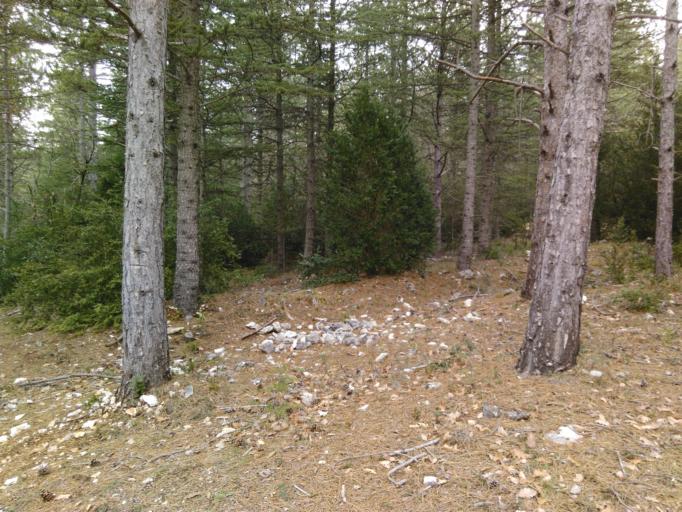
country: FR
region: Provence-Alpes-Cote d'Azur
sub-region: Departement du Vaucluse
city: Villes-sur-Auzon
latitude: 44.1166
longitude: 5.2668
